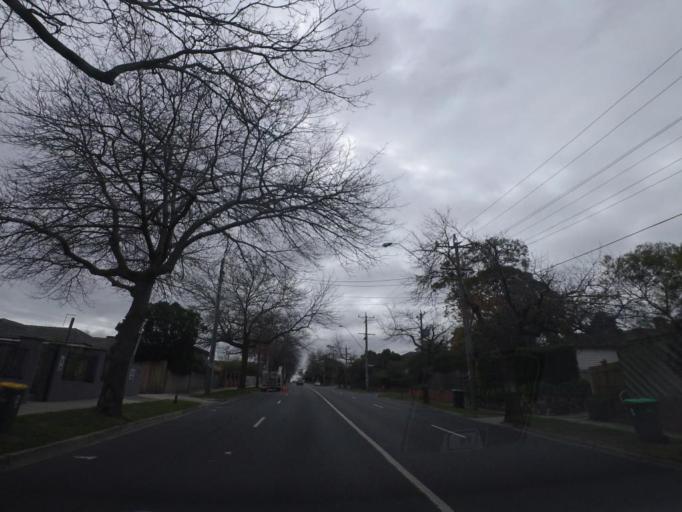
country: AU
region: Victoria
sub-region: Whitehorse
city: Box Hill South
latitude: -37.8343
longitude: 145.1120
